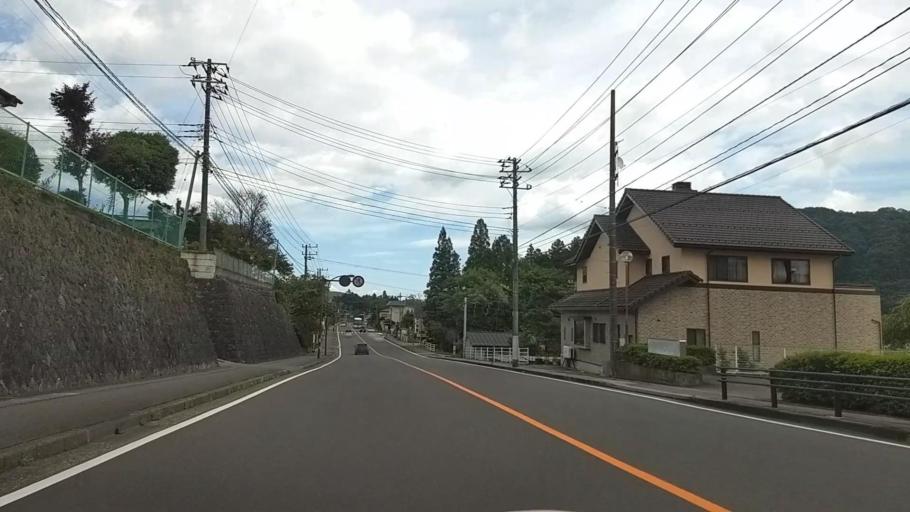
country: JP
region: Tochigi
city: Nikko
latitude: 36.7509
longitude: 139.5825
